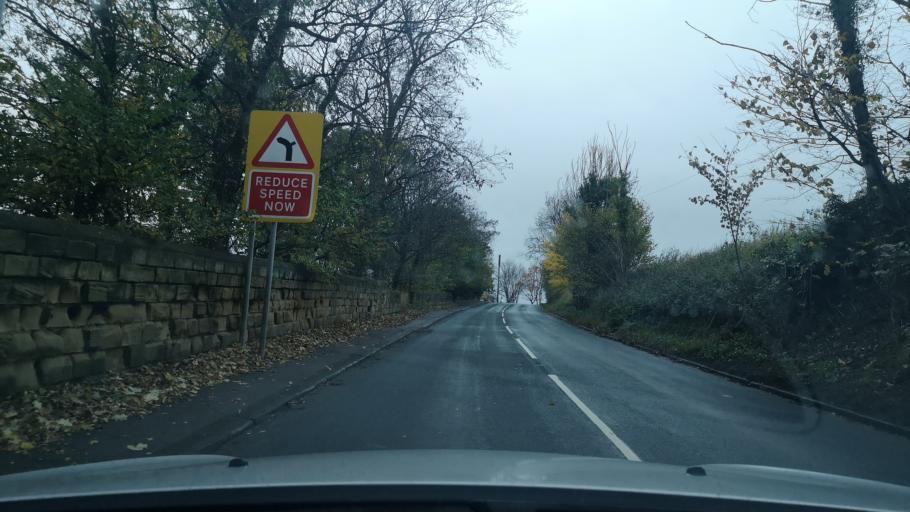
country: GB
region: England
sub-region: City and Borough of Wakefield
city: Low Ackworth
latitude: 53.6644
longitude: -1.3261
